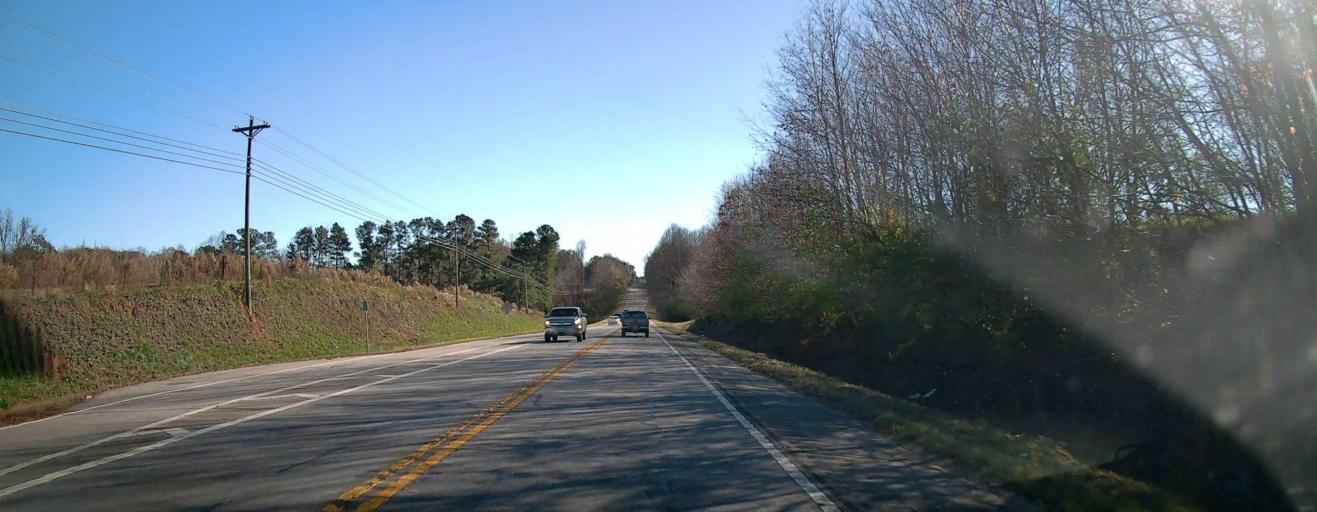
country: US
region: Georgia
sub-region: White County
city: Cleveland
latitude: 34.5340
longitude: -83.7571
